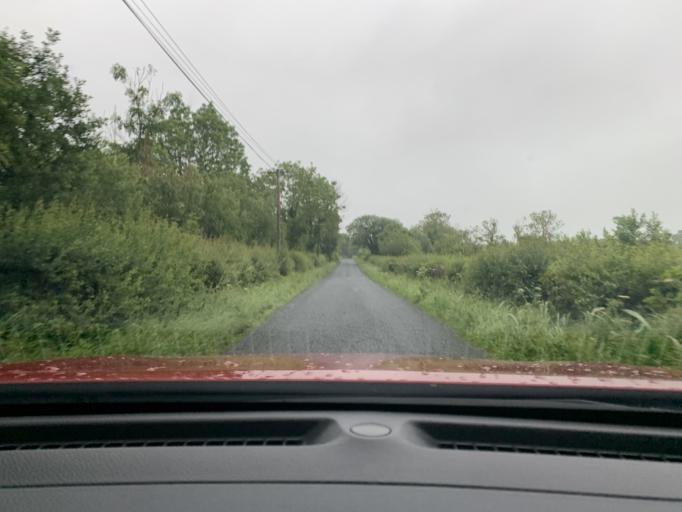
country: IE
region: Connaught
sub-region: Sligo
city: Sligo
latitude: 54.3199
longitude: -8.4735
